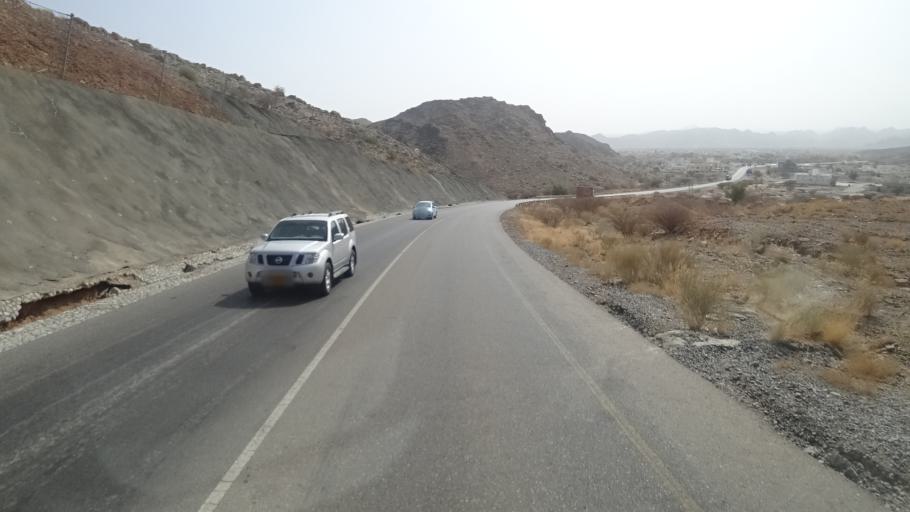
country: OM
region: Muhafazat ad Dakhiliyah
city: Nizwa
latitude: 23.0043
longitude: 57.5676
